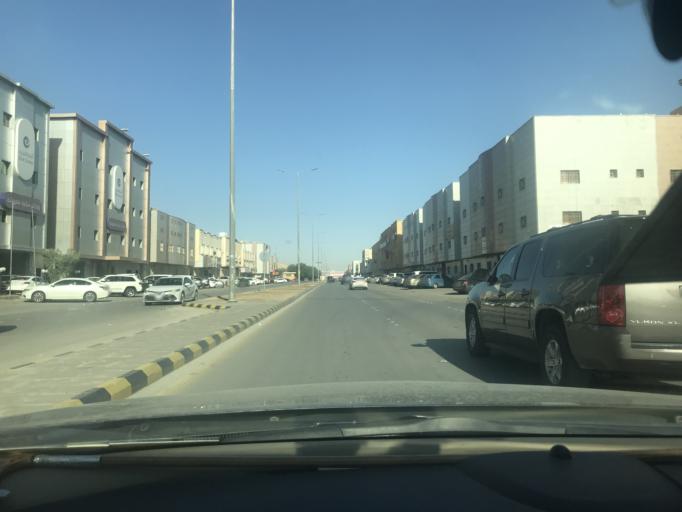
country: SA
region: Ar Riyad
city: Riyadh
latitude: 24.7514
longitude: 46.6703
